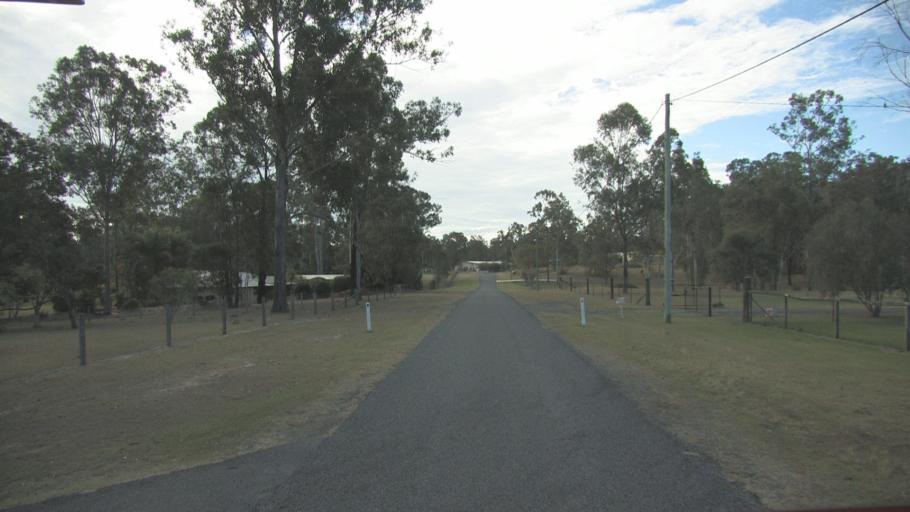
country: AU
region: Queensland
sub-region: Logan
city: North Maclean
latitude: -27.8221
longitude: 153.0488
